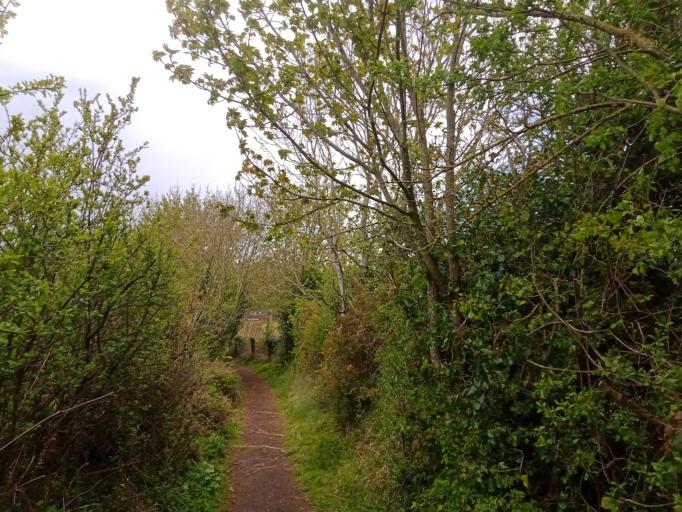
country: IE
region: Leinster
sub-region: Kilkenny
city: Kilkenny
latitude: 52.6928
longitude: -7.2669
